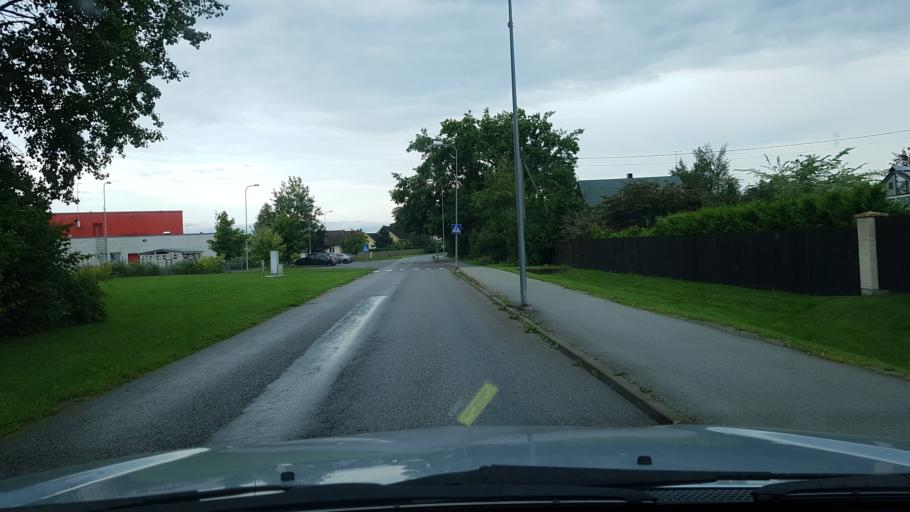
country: EE
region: Harju
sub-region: Rae vald
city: Jueri
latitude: 59.3519
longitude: 24.9066
